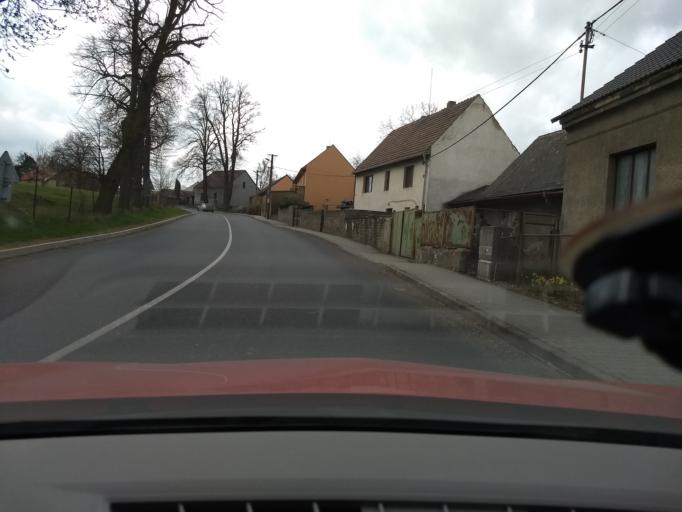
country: CZ
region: Central Bohemia
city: Unhost'
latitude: 50.1087
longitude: 14.1353
